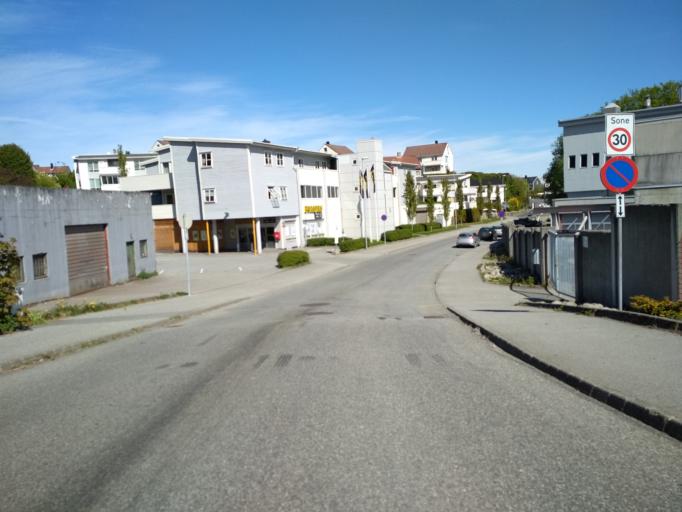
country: NO
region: Rogaland
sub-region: Stavanger
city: Stavanger
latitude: 58.9748
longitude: 5.7119
